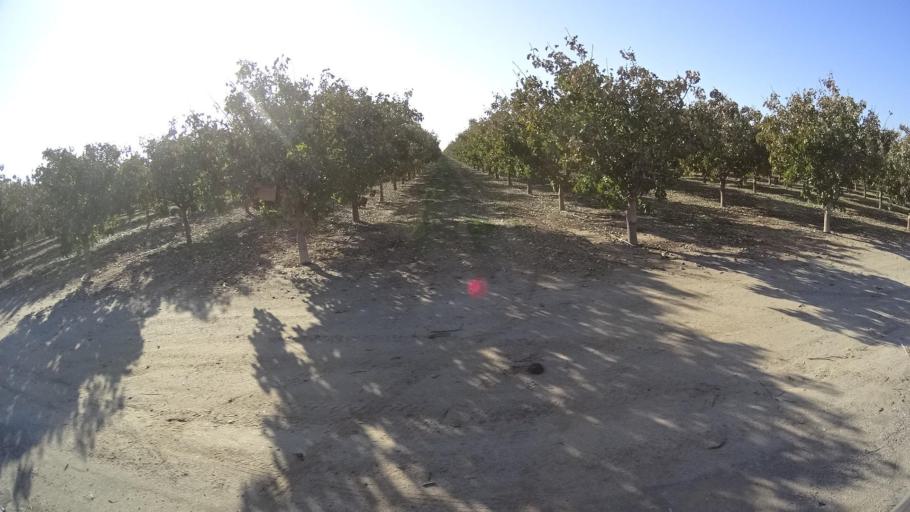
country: US
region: California
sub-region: Tulare County
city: Richgrove
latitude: 35.7327
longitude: -119.1188
